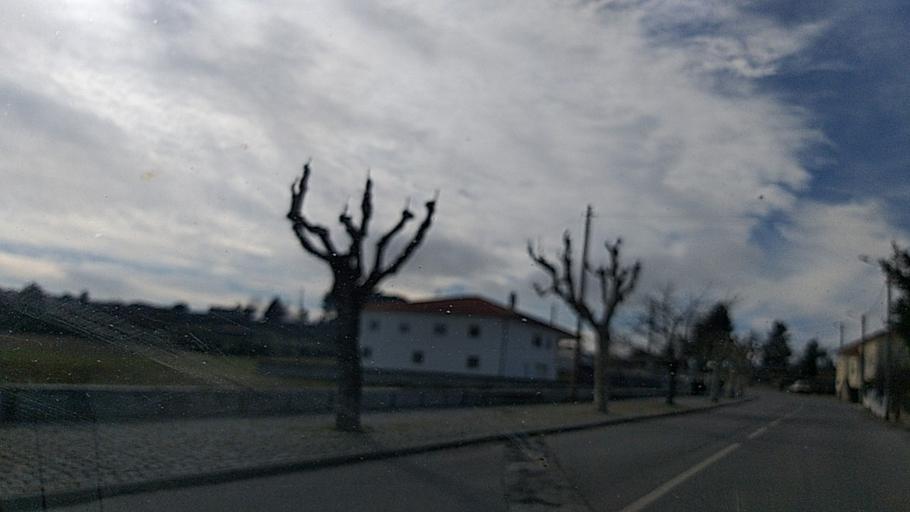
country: PT
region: Guarda
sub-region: Fornos de Algodres
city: Fornos de Algodres
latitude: 40.6789
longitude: -7.5302
